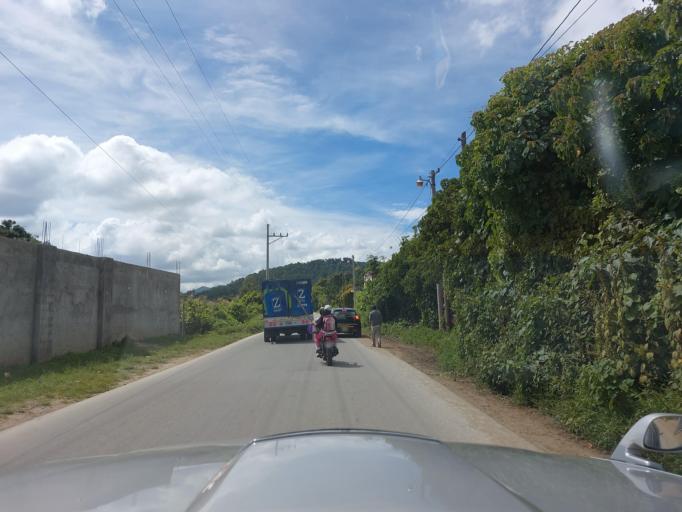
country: GT
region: Chimaltenango
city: San Andres Itzapa
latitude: 14.6194
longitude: -90.8339
